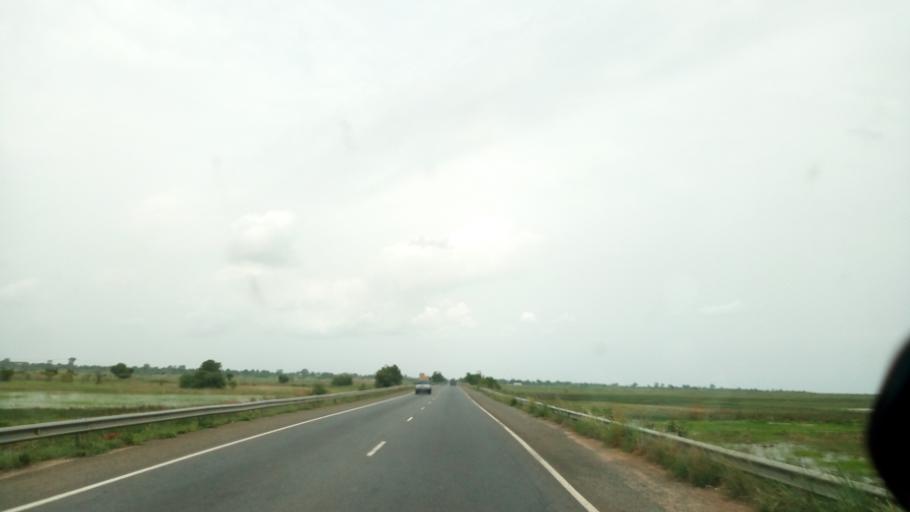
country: GH
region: Volta
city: Keta
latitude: 6.0630
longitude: 0.9256
